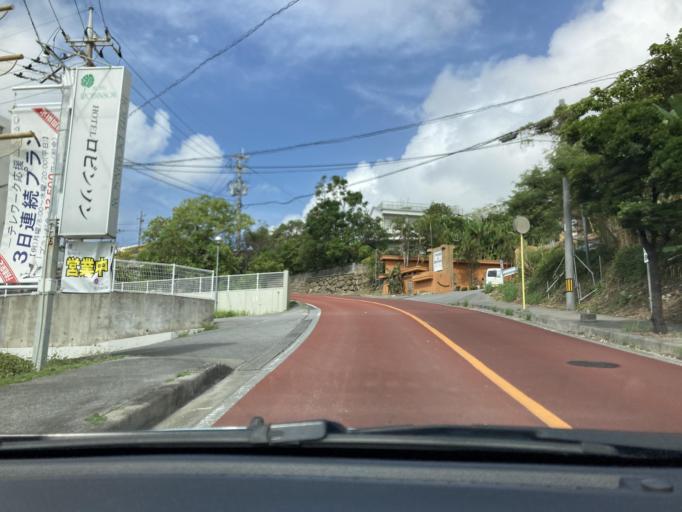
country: JP
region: Okinawa
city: Okinawa
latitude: 26.3208
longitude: 127.8095
